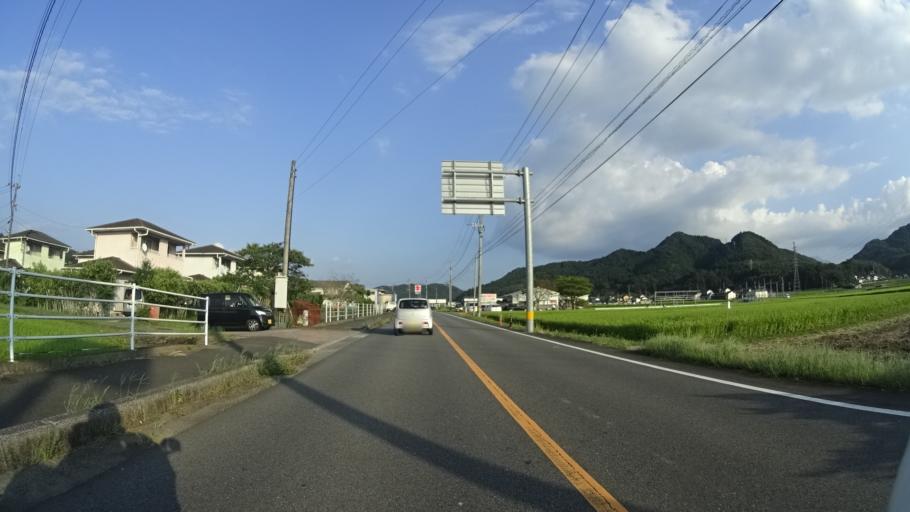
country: JP
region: Oita
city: Bungo-Takada-shi
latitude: 33.4362
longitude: 131.3619
